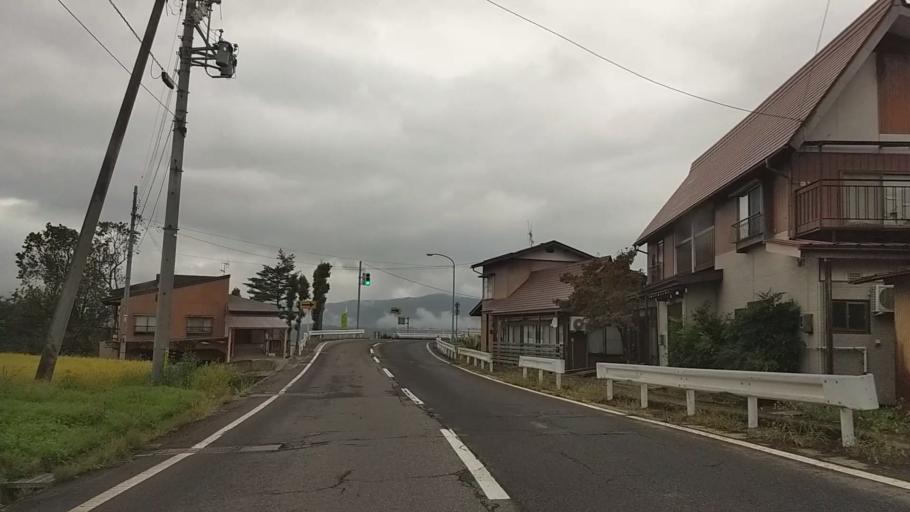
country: JP
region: Nagano
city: Iiyama
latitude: 36.8435
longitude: 138.4057
